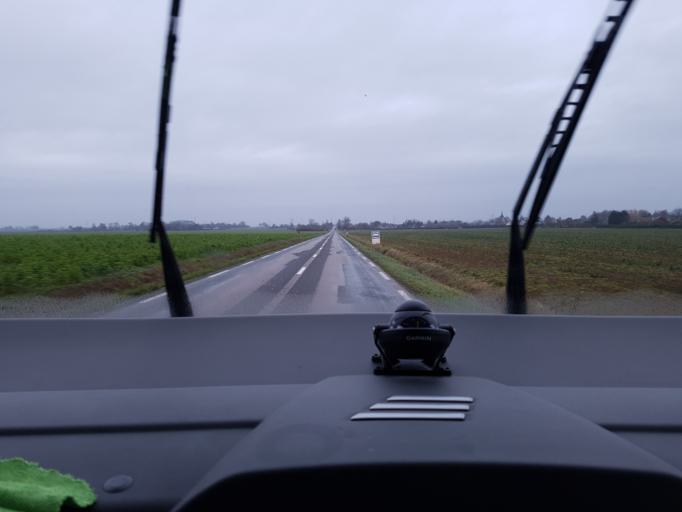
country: FR
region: Haute-Normandie
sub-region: Departement de l'Eure
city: Beaumont-le-Roger
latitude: 49.1058
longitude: 0.8308
